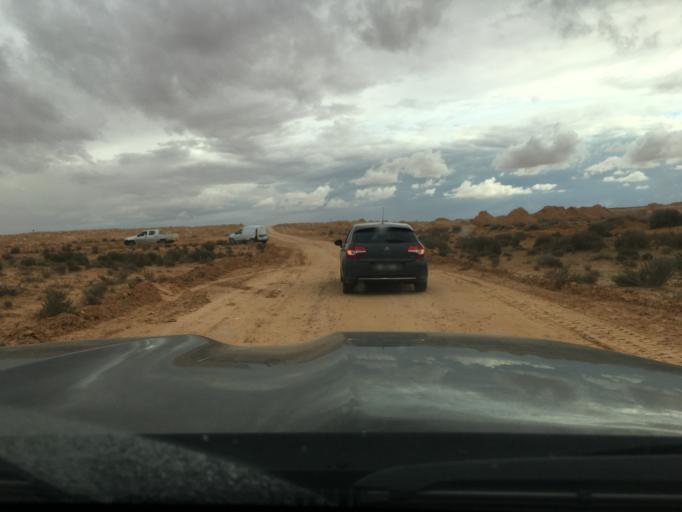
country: TN
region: Madanin
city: Medenine
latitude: 33.2598
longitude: 10.5734
